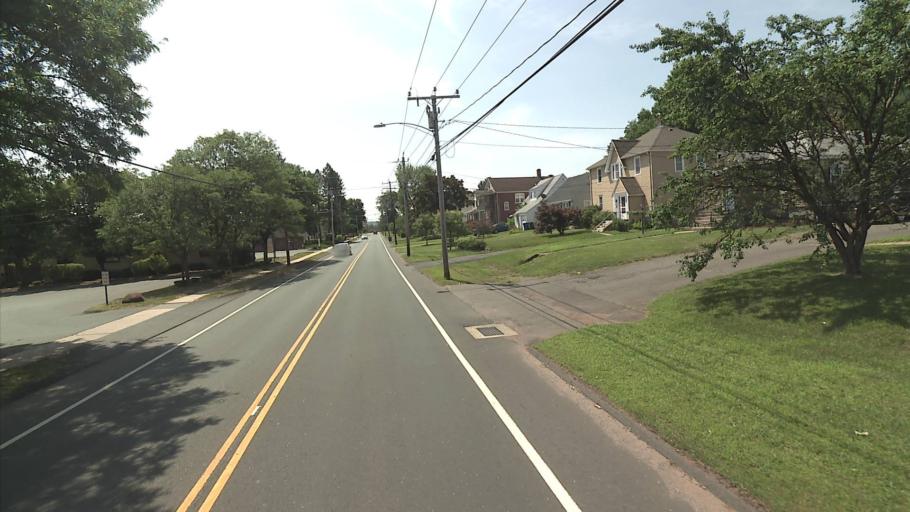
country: US
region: Connecticut
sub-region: Hartford County
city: Kensington
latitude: 41.6394
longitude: -72.7696
